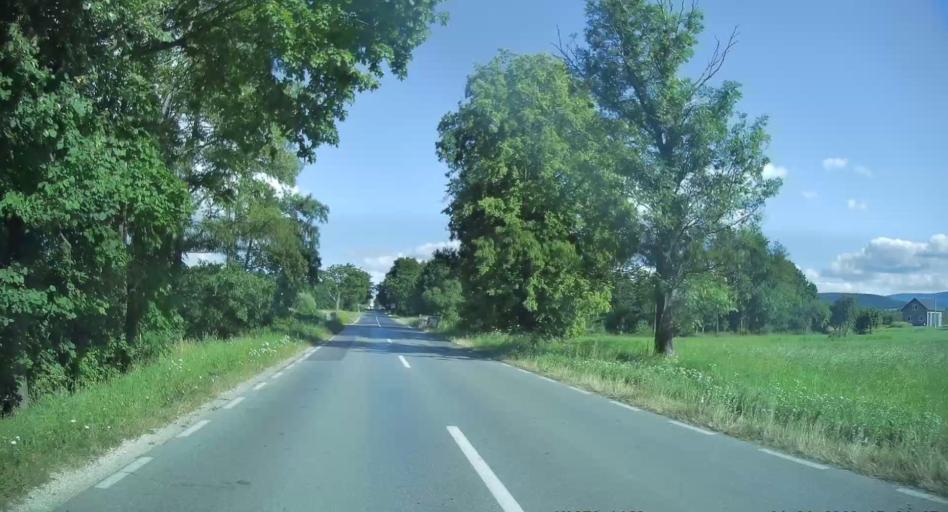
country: PL
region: Swietokrzyskie
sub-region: Powiat kielecki
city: Bodzentyn
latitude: 50.9611
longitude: 20.9034
